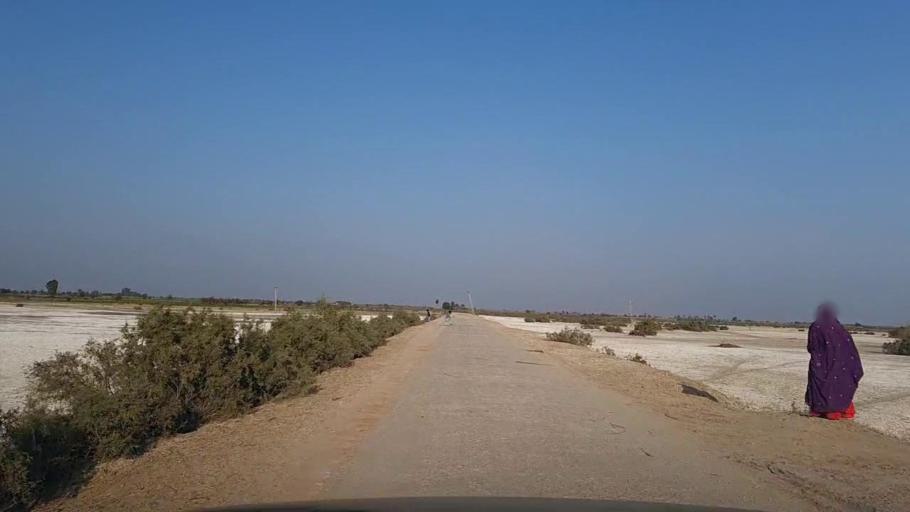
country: PK
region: Sindh
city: Tando Mittha Khan
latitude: 25.9299
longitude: 69.0654
